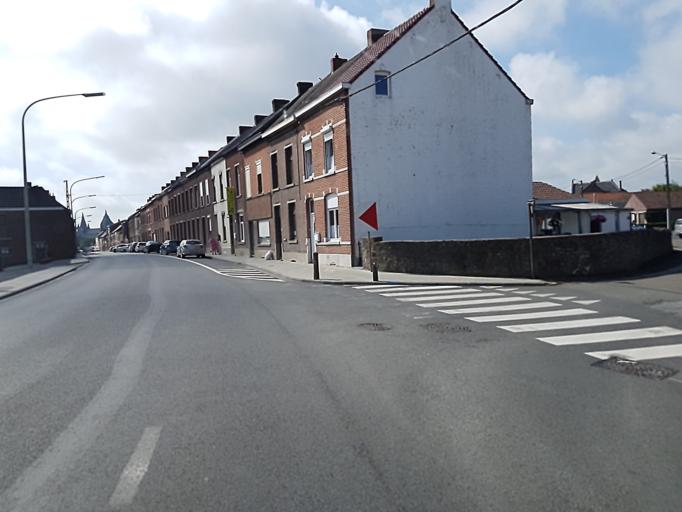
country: BE
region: Wallonia
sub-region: Province du Hainaut
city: Soignies
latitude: 50.5855
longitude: 4.0642
